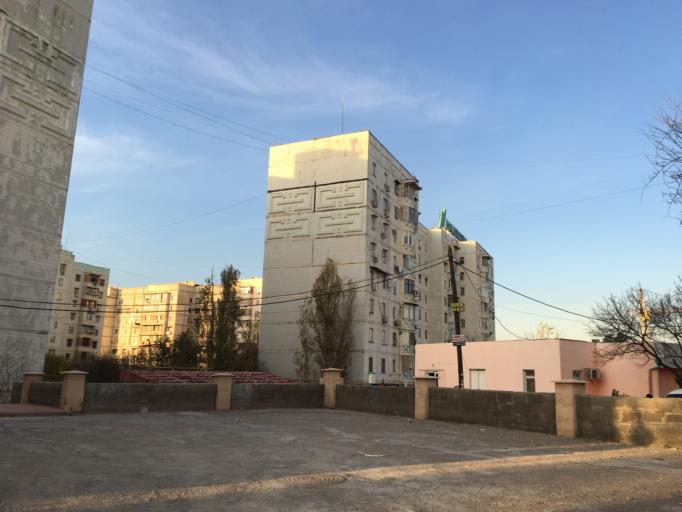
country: UZ
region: Toshkent
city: Salor
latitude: 41.3122
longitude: 69.3294
